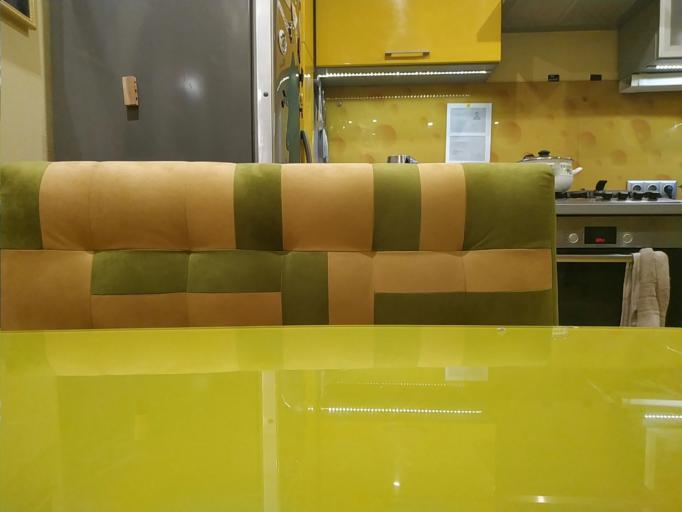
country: RU
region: Murmansk
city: Alakurtti
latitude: 66.2133
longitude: 30.2841
